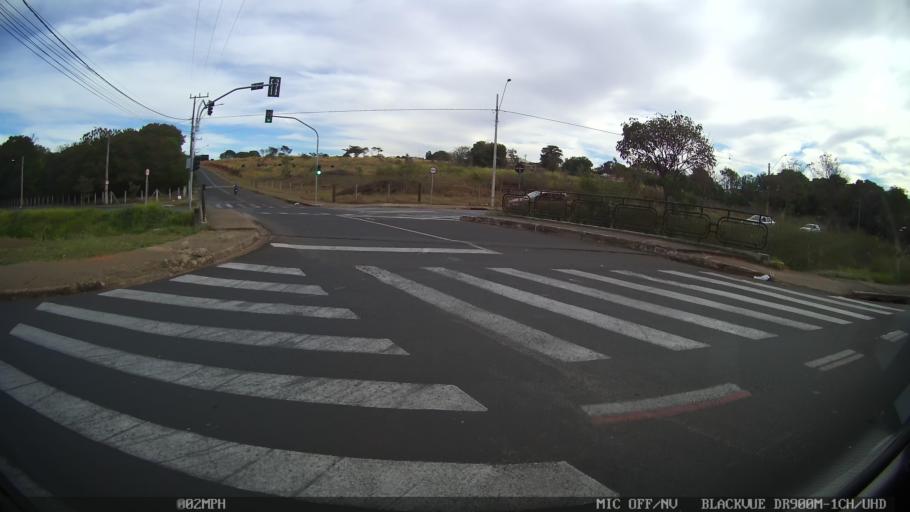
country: BR
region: Sao Paulo
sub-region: Catanduva
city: Catanduva
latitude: -21.1332
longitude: -48.9873
